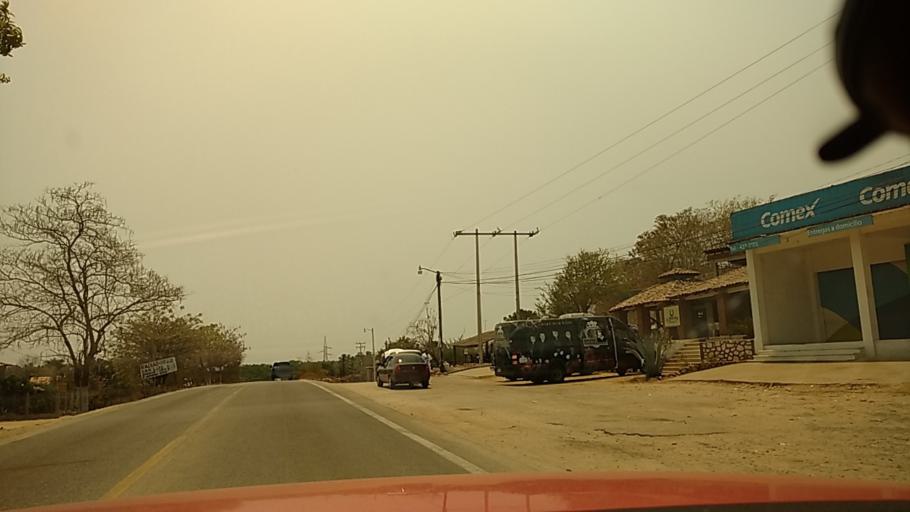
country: MX
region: Guerrero
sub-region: Tecpan de Galeana
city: Villa Rotaria
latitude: 17.2667
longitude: -100.8786
